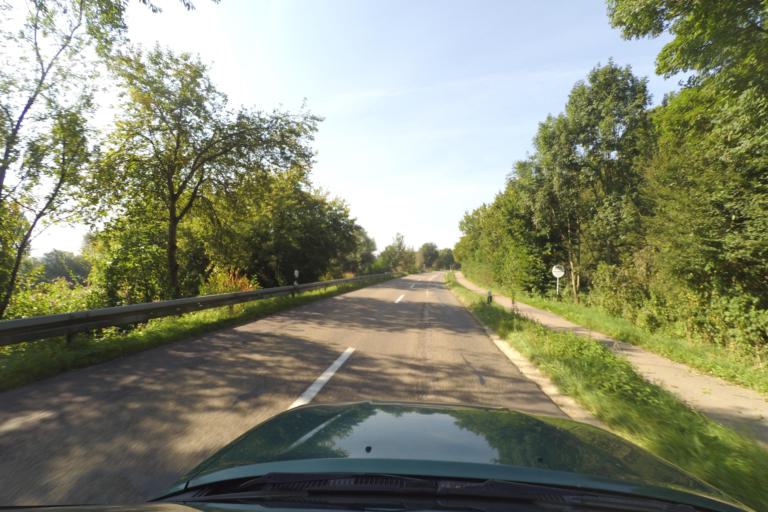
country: DE
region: Bavaria
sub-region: Swabia
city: Genderkingen
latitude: 48.7204
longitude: 10.8499
